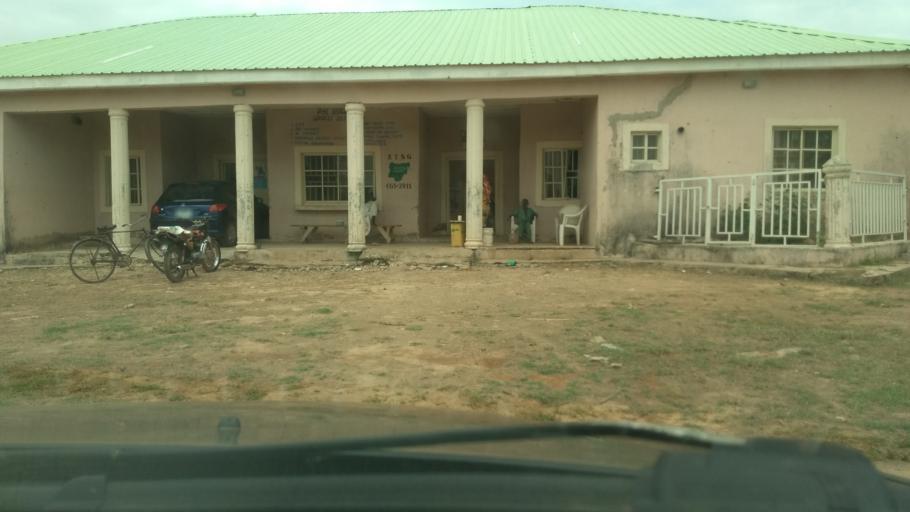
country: NG
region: Katsina
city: Kankia
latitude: 12.4081
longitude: 7.7212
